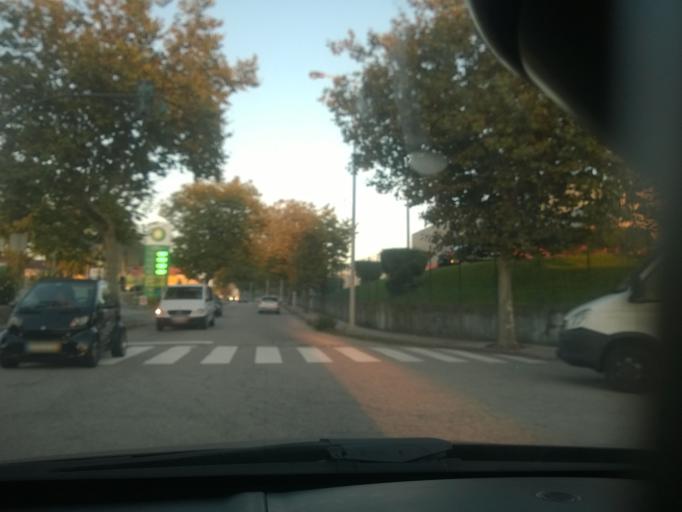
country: PT
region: Porto
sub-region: Matosinhos
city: Santa Cruz do Bispo
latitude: 41.2224
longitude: -8.7039
